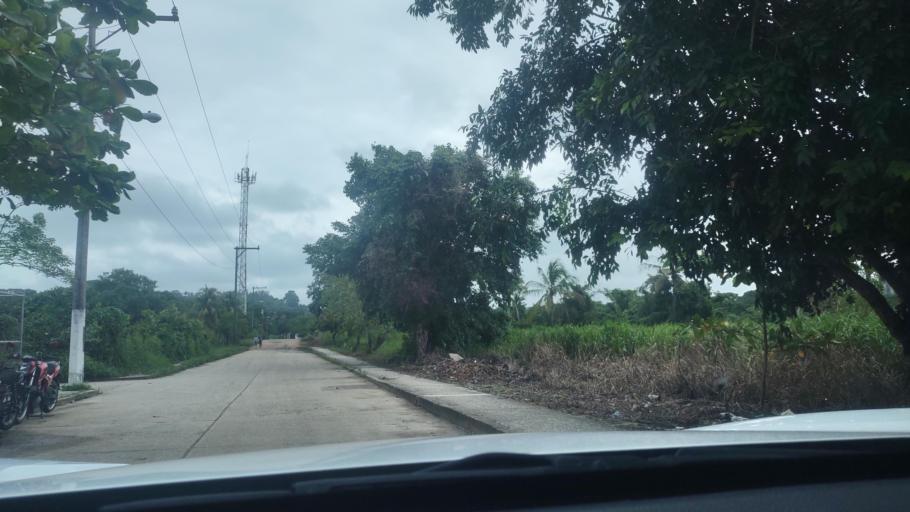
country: MX
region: Veracruz
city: Villa Nanchital
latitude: 18.0420
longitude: -94.3500
